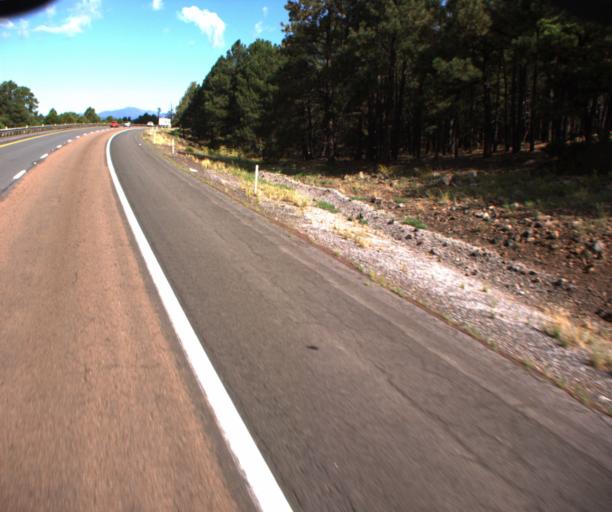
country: US
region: Arizona
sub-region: Coconino County
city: Flagstaff
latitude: 35.2039
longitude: -111.7662
